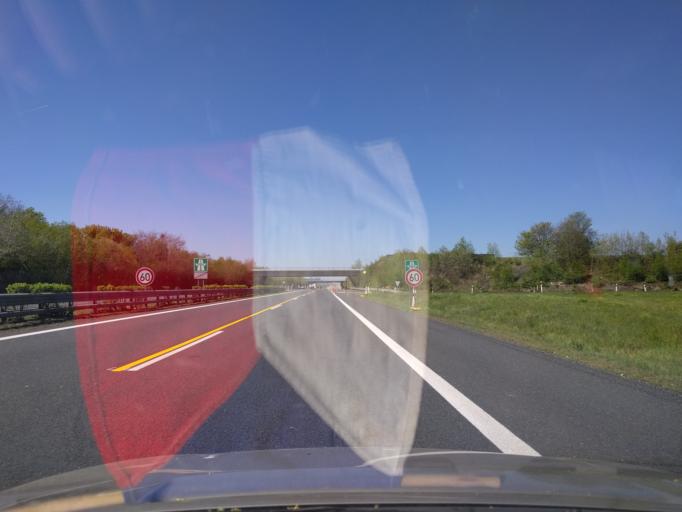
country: CZ
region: Central Bohemia
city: Jirny
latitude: 50.1228
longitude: 14.7072
